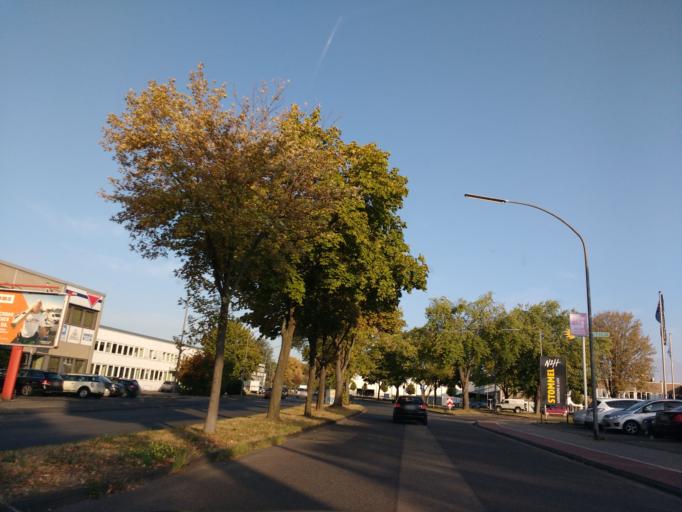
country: DE
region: North Rhine-Westphalia
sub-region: Regierungsbezirk Koln
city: Bilderstoeckchen
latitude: 50.9818
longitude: 6.9170
